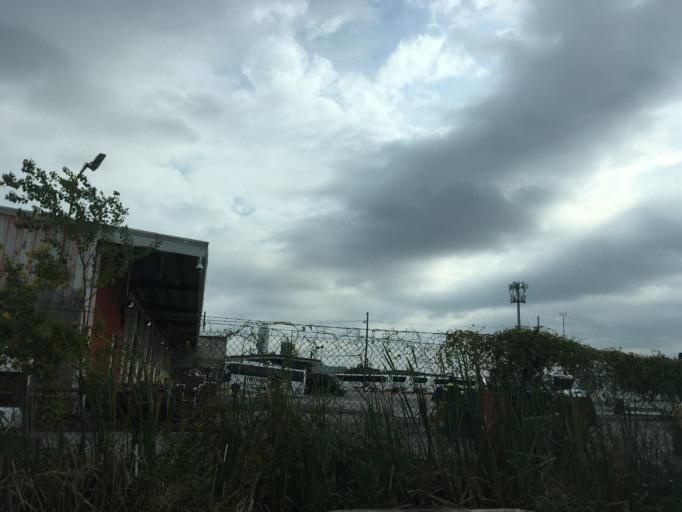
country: US
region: Louisiana
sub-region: Orleans Parish
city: New Orleans
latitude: 29.9871
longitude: -90.0619
